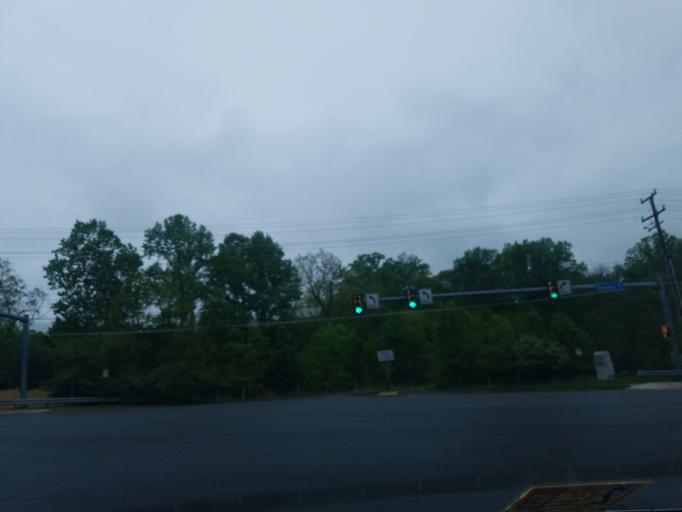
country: US
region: Virginia
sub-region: Fairfax County
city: Herndon
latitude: 38.9922
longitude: -77.3765
